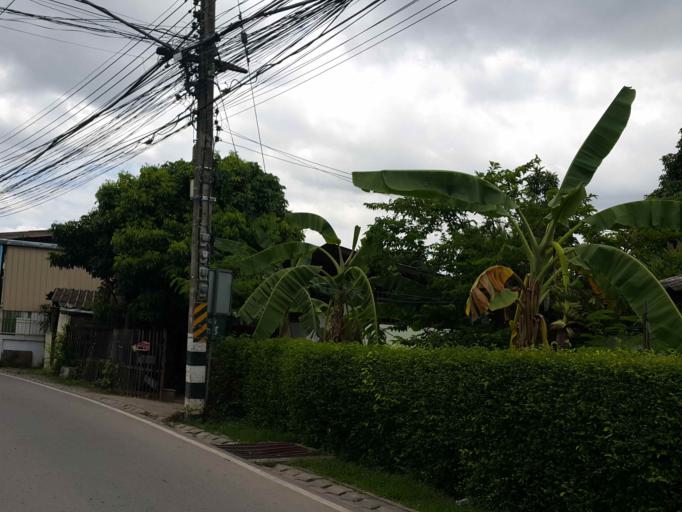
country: TH
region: Chiang Mai
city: Chiang Mai
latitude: 18.8131
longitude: 99.0054
